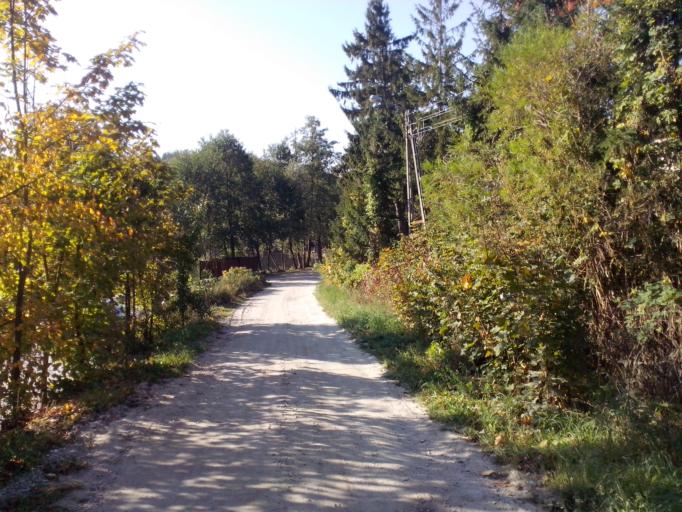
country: PL
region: Kujawsko-Pomorskie
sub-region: Powiat brodnicki
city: Gorzno
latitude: 53.1975
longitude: 19.6588
